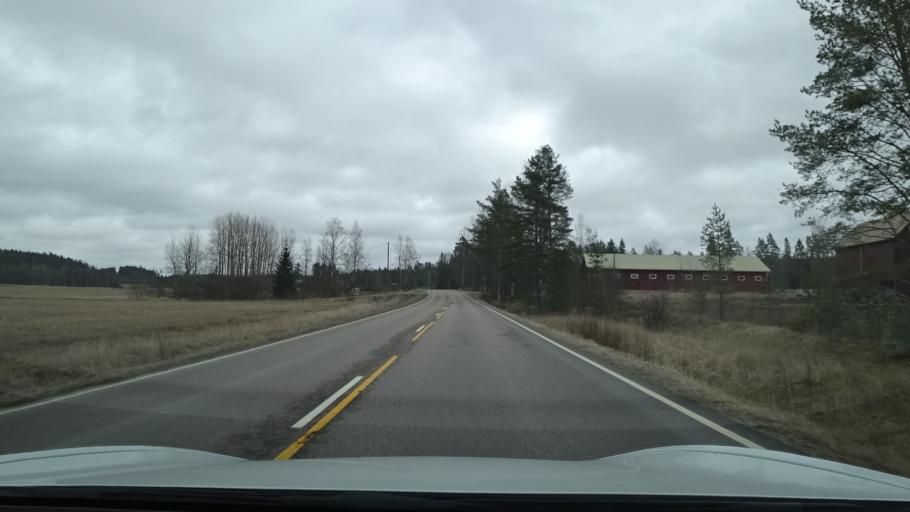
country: FI
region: Uusimaa
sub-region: Porvoo
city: Myrskylae
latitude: 60.7128
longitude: 25.9427
